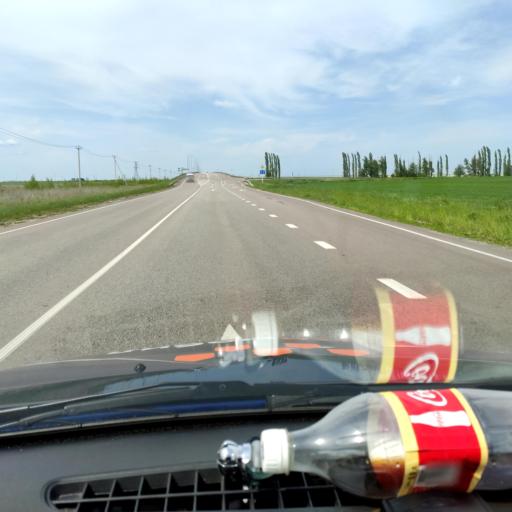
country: RU
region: Voronezj
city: Novaya Usman'
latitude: 51.5848
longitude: 39.3745
